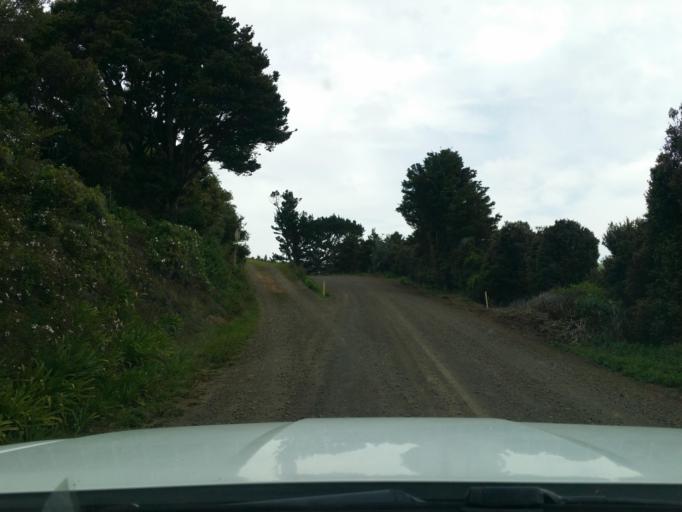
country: NZ
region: Northland
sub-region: Kaipara District
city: Dargaville
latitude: -35.7326
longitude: 173.5943
